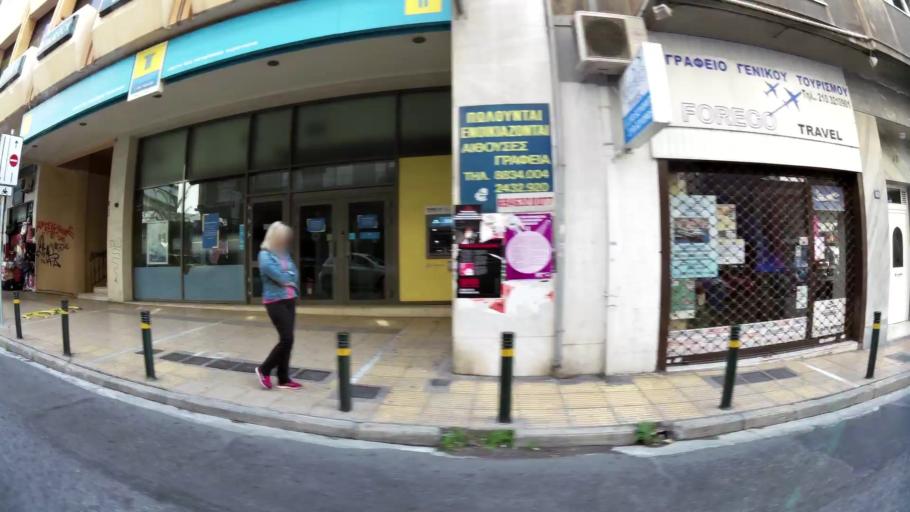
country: GR
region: Attica
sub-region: Nomarchia Athinas
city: Kipseli
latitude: 37.9999
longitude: 23.7394
